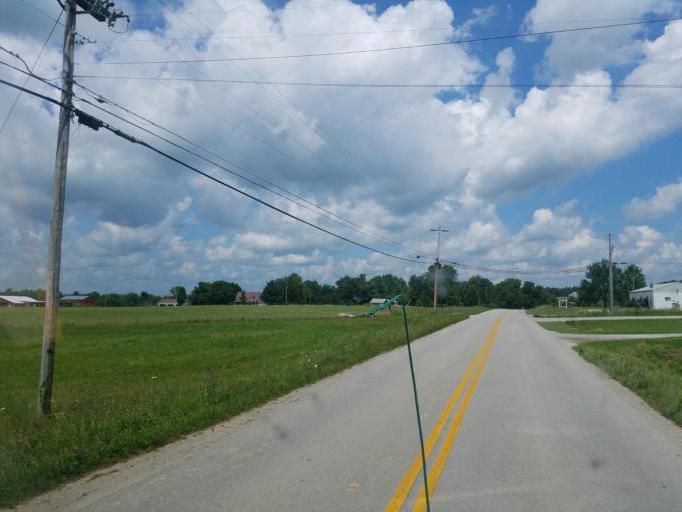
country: US
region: Kentucky
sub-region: Grayson County
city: Leitchfield
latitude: 37.5168
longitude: -86.3288
